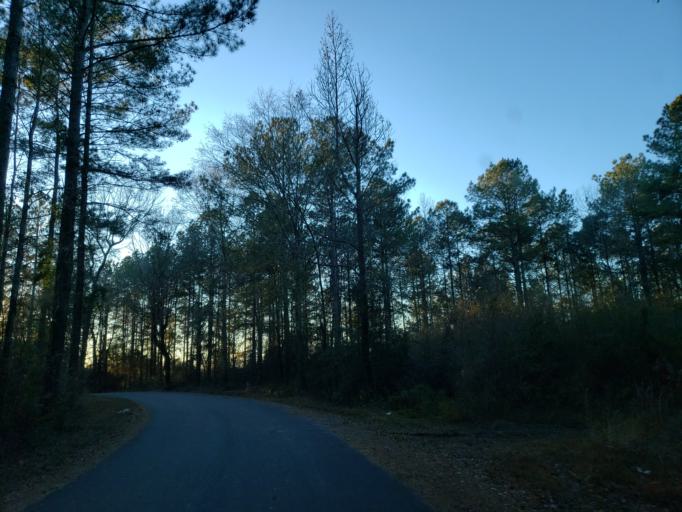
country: US
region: Mississippi
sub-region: Covington County
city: Collins
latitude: 31.5707
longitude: -89.4414
